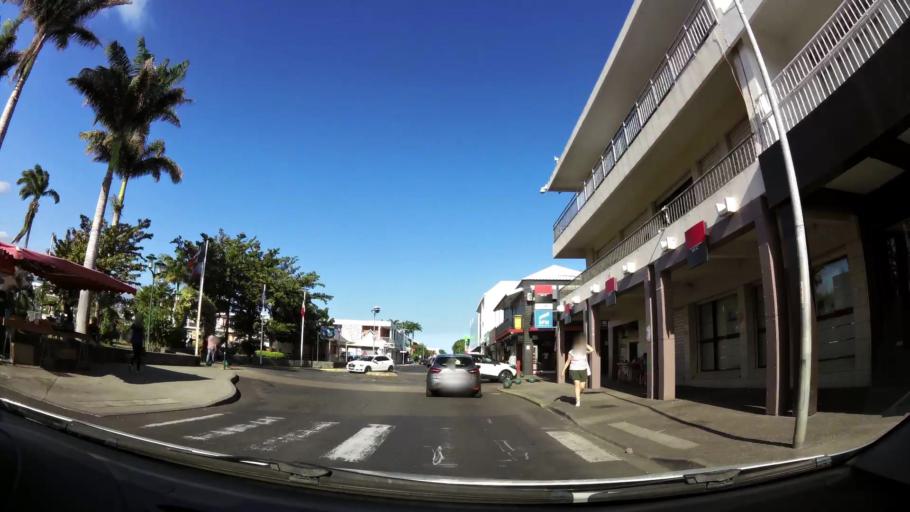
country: RE
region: Reunion
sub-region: Reunion
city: Saint-Louis
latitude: -21.2871
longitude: 55.4086
